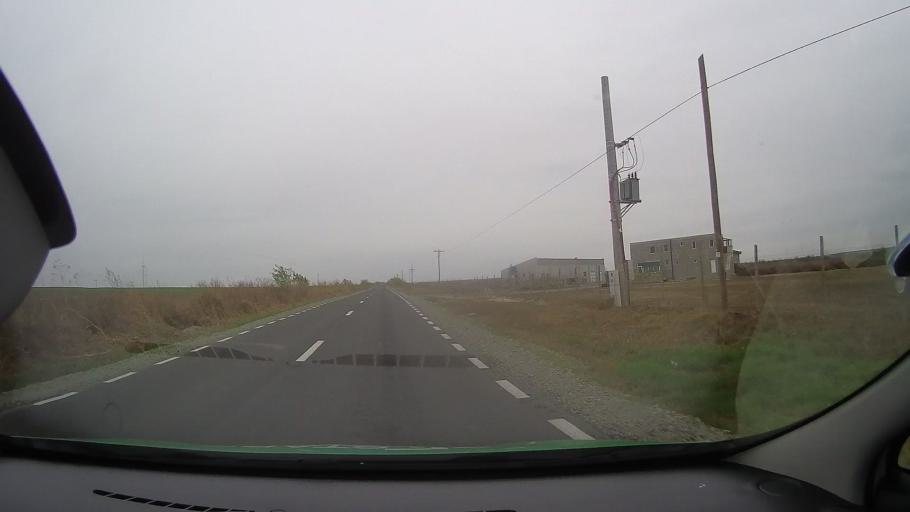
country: RO
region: Constanta
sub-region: Comuna Tortoman
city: Tortoman
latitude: 44.3668
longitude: 28.2081
